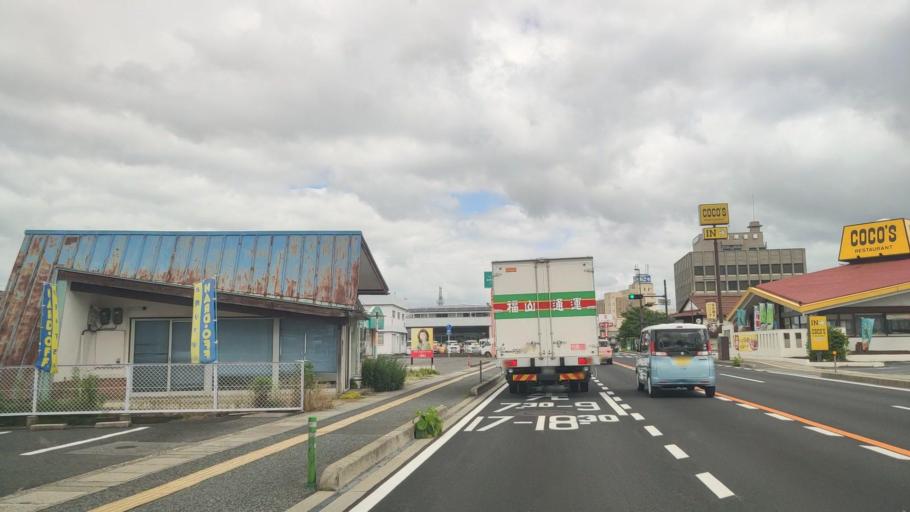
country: JP
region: Tottori
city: Yonago
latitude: 35.4367
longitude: 133.3452
